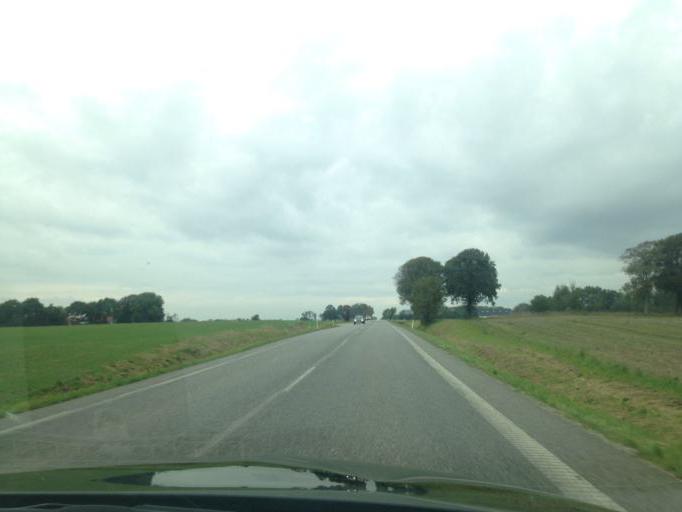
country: DK
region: South Denmark
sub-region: Kolding Kommune
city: Christiansfeld
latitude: 55.4189
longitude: 9.4768
